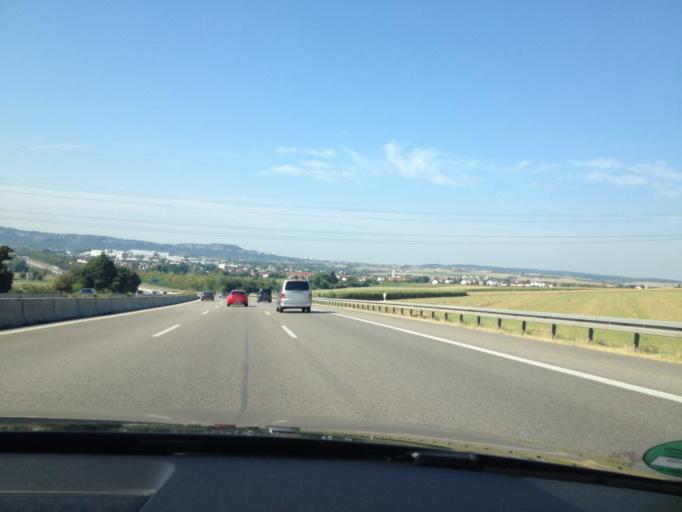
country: DE
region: Baden-Wuerttemberg
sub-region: Regierungsbezirk Stuttgart
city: Ditzingen
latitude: 48.8350
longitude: 9.0926
